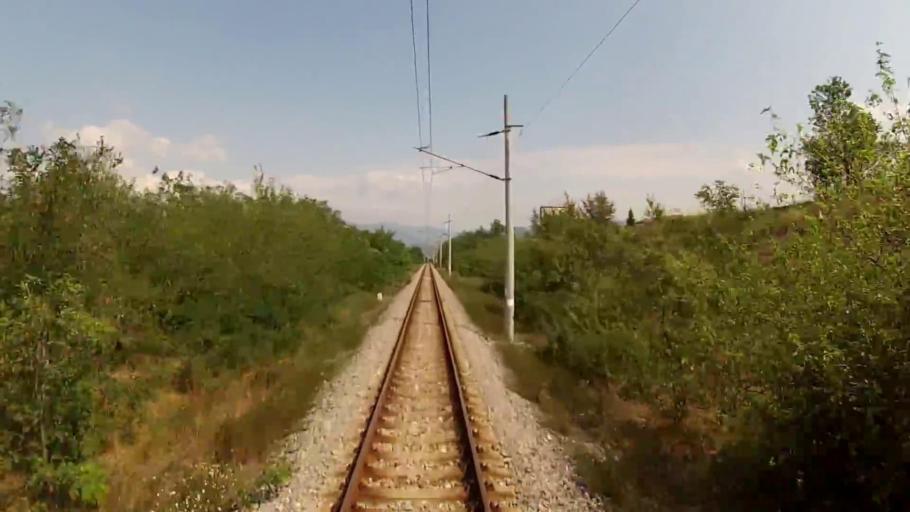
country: BG
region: Blagoevgrad
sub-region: Obshtina Strumyani
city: Strumyani
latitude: 41.6670
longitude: 23.1820
